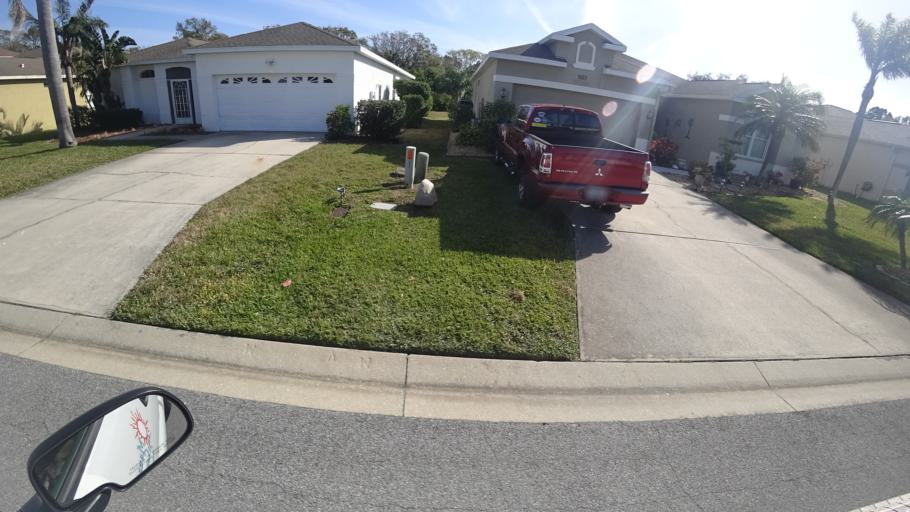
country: US
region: Florida
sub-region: Manatee County
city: South Bradenton
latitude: 27.4536
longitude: -82.6056
